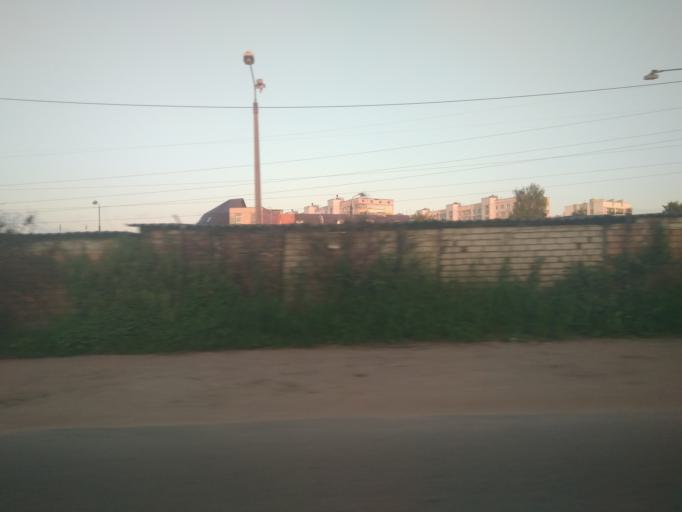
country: BY
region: Minsk
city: Novoye Medvezhino
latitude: 53.9213
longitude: 27.4706
